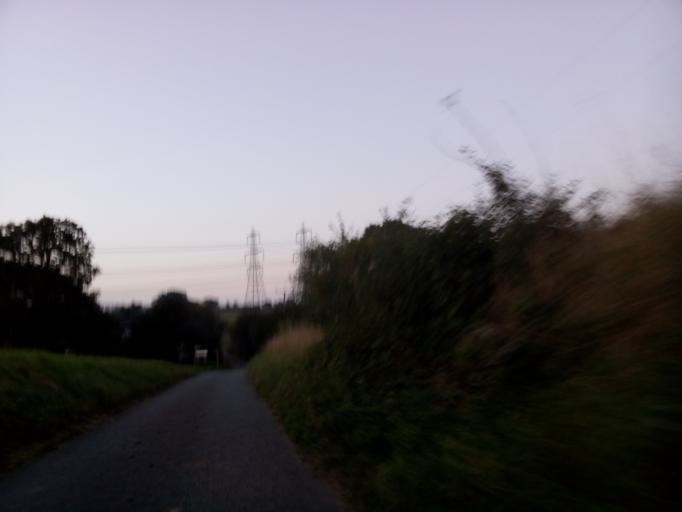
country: GB
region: England
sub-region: Suffolk
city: Kesgrave
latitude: 52.1118
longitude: 1.2340
